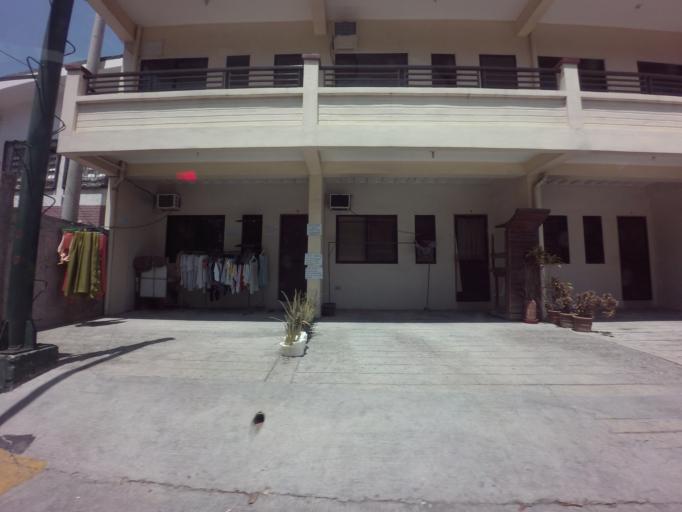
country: PH
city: Sambayanihan People's Village
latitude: 14.4247
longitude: 121.0125
